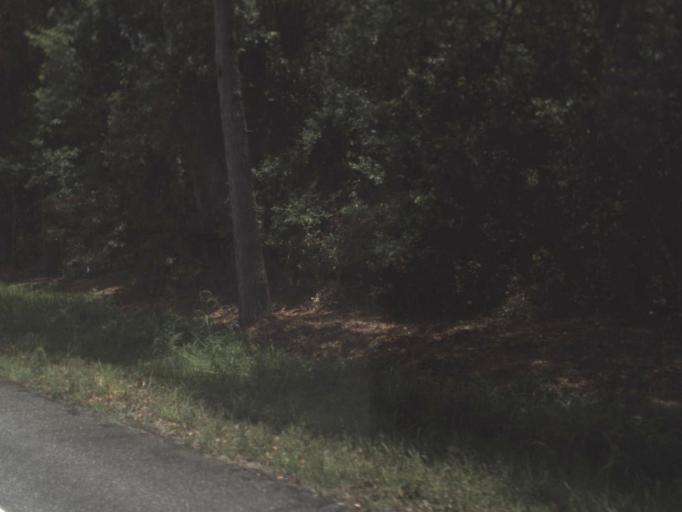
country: US
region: Florida
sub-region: Lafayette County
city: Mayo
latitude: 29.9683
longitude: -83.2194
